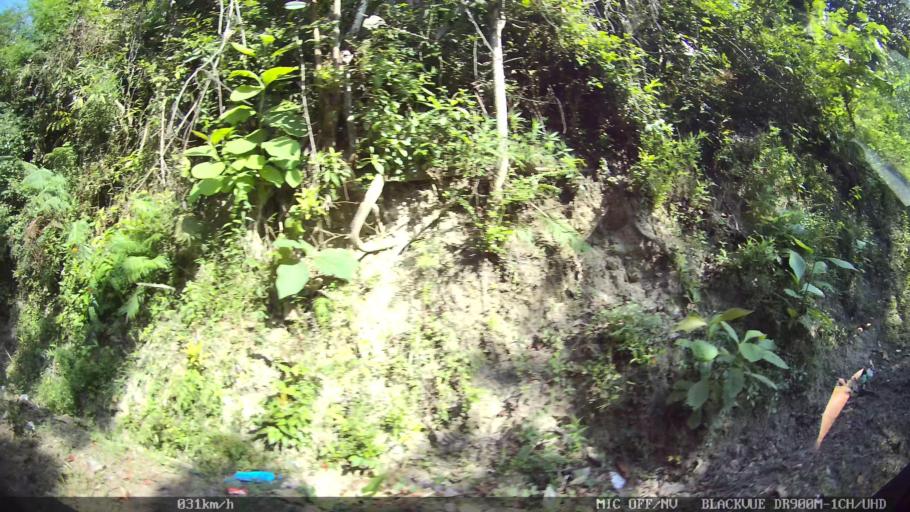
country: ID
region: Daerah Istimewa Yogyakarta
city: Kasihan
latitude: -7.8302
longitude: 110.2880
